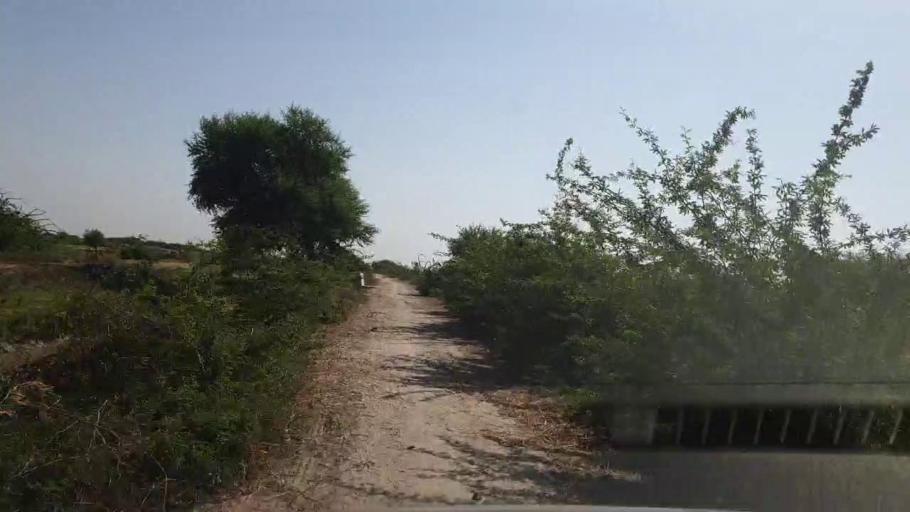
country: PK
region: Sindh
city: Kadhan
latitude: 24.6201
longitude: 68.9962
